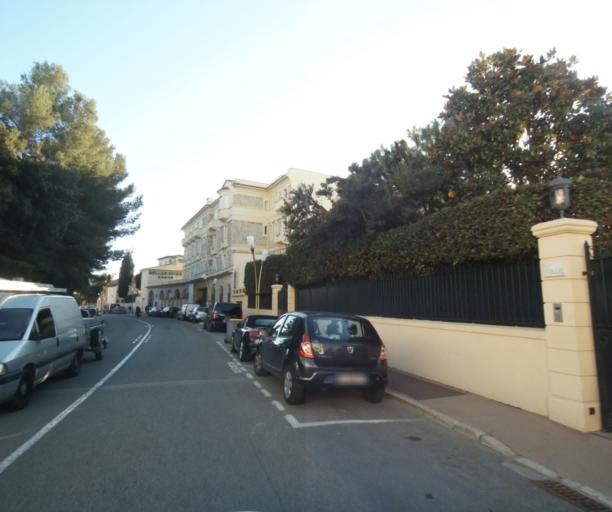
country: FR
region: Provence-Alpes-Cote d'Azur
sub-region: Departement des Alpes-Maritimes
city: Antibes
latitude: 43.5652
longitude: 7.1156
